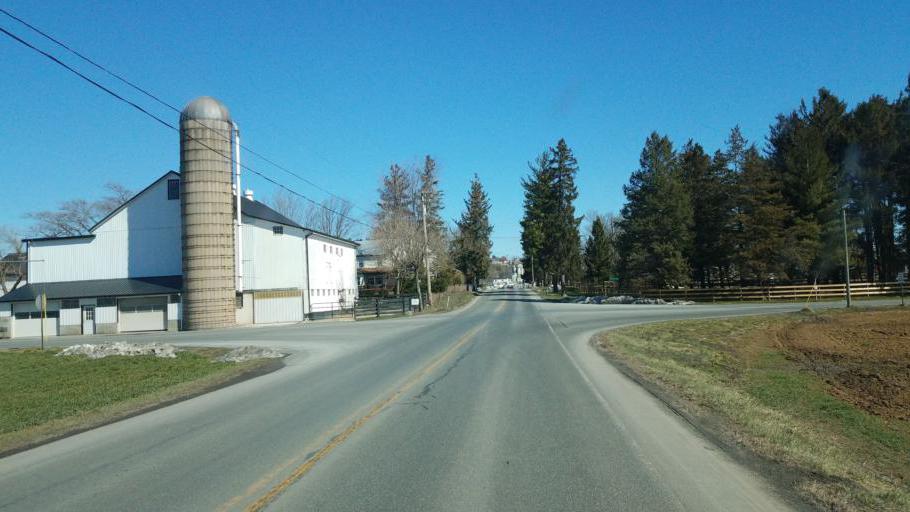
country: US
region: Pennsylvania
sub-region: Lancaster County
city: Terre Hill
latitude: 40.1473
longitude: -76.0463
